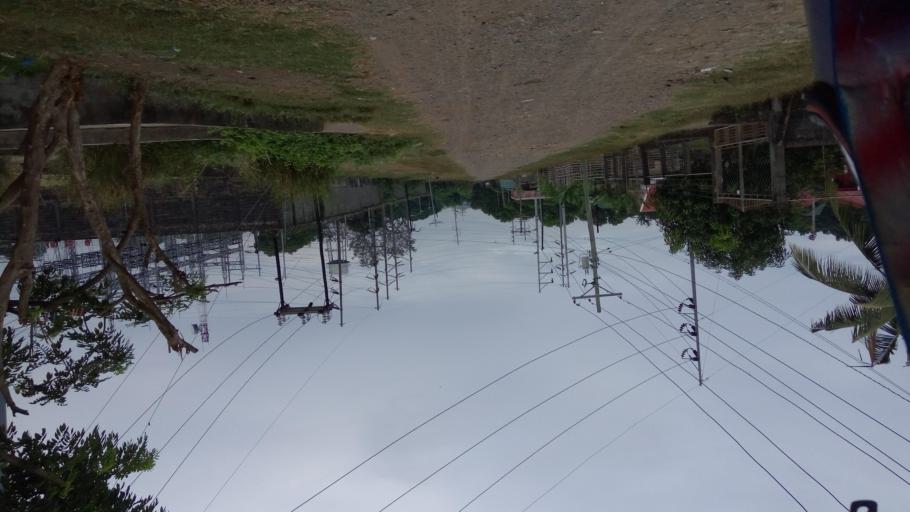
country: PH
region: Ilocos
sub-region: Province of La Union
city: Paringao
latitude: 16.5556
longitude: 120.3256
